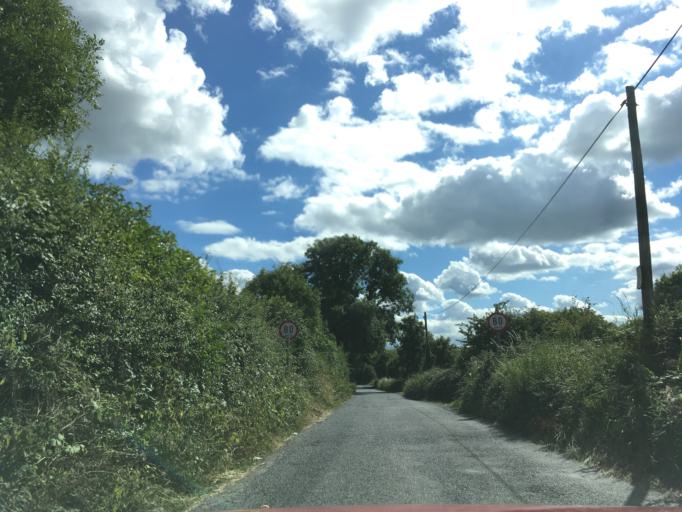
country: IE
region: Munster
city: Cashel
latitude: 52.5053
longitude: -7.8958
